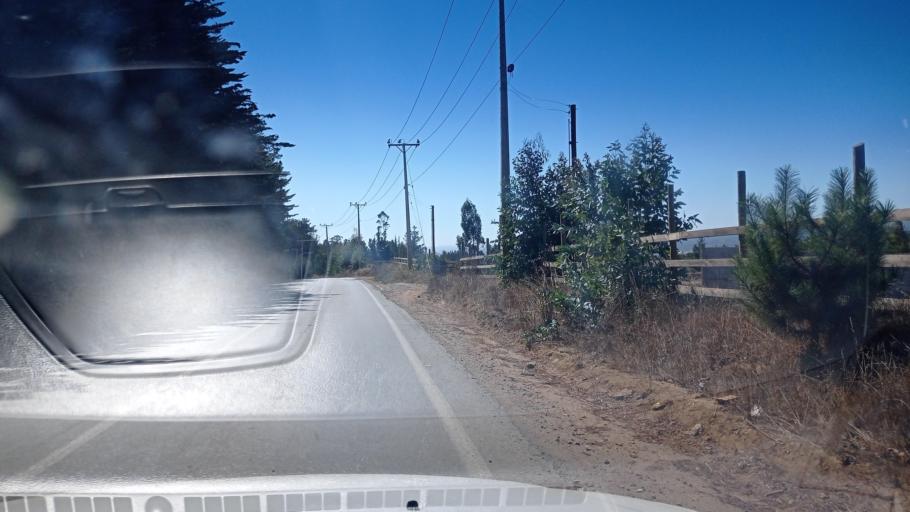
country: CL
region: O'Higgins
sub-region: Provincia de Colchagua
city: Santa Cruz
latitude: -34.4206
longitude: -72.0012
